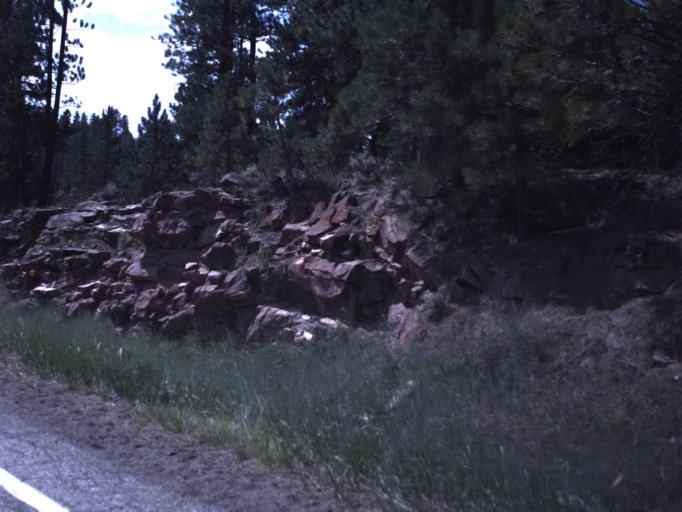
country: US
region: Utah
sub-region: Daggett County
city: Manila
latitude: 40.8586
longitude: -109.6854
